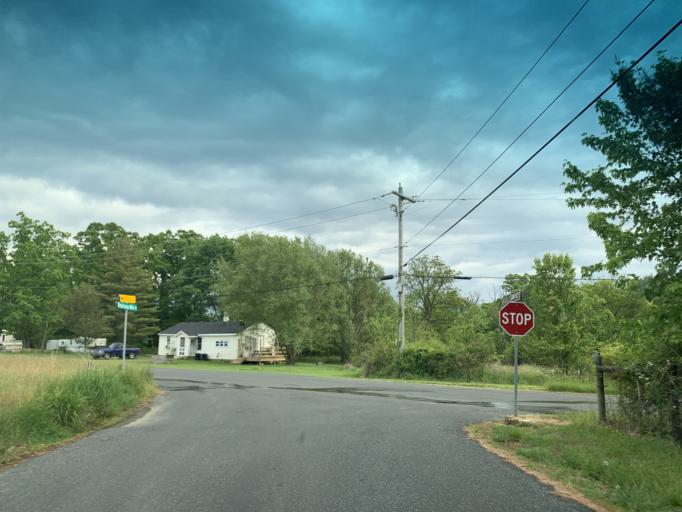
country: US
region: Pennsylvania
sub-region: York County
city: Susquehanna Trails
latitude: 39.6717
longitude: -76.2579
